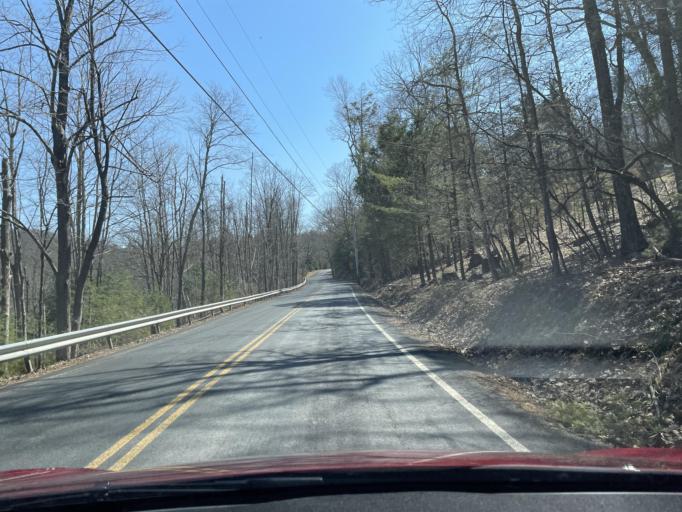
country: US
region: New York
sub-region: Ulster County
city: Woodstock
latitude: 42.0088
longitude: -74.1620
